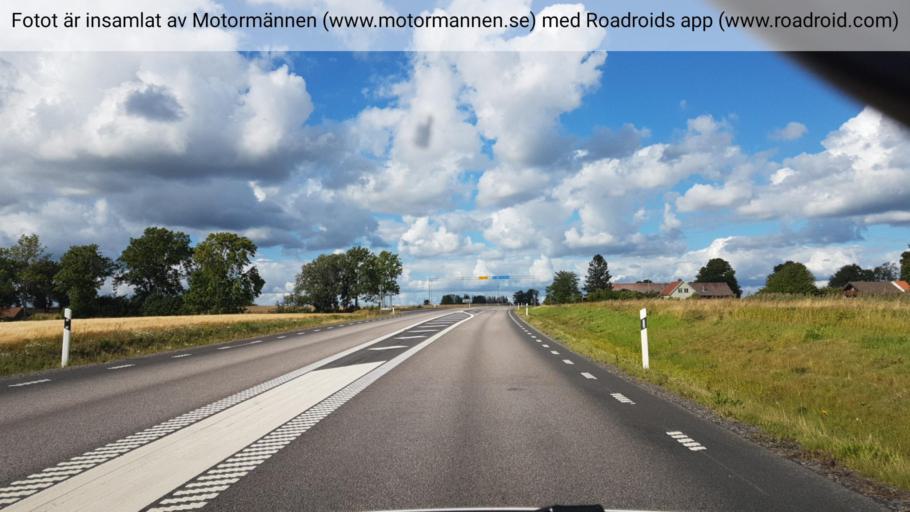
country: SE
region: Vaestra Goetaland
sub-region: Falkopings Kommun
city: Falkoeping
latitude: 58.2071
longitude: 13.5603
